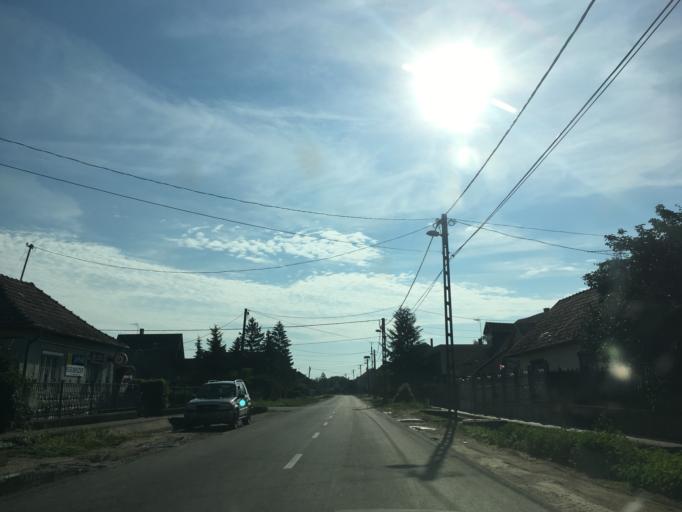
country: HU
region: Szabolcs-Szatmar-Bereg
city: Nyirbeltek
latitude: 47.6951
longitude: 22.1190
